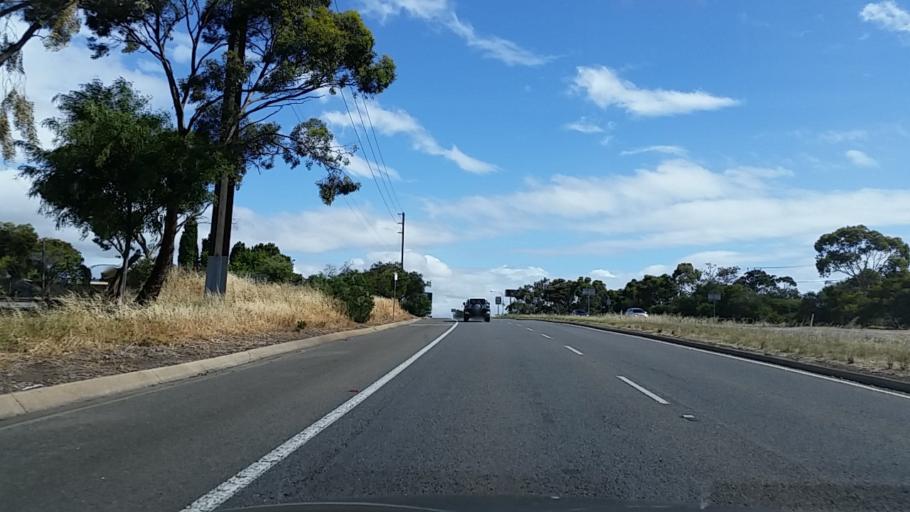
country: AU
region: South Australia
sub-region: Adelaide
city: Port Noarlunga
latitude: -35.1273
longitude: 138.4857
